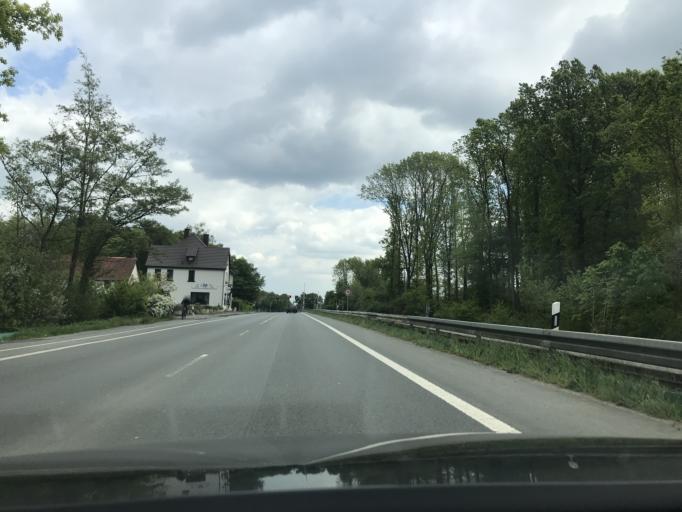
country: DE
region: North Rhine-Westphalia
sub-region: Regierungsbezirk Detmold
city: Rheda-Wiedenbruck
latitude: 51.8670
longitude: 8.2645
